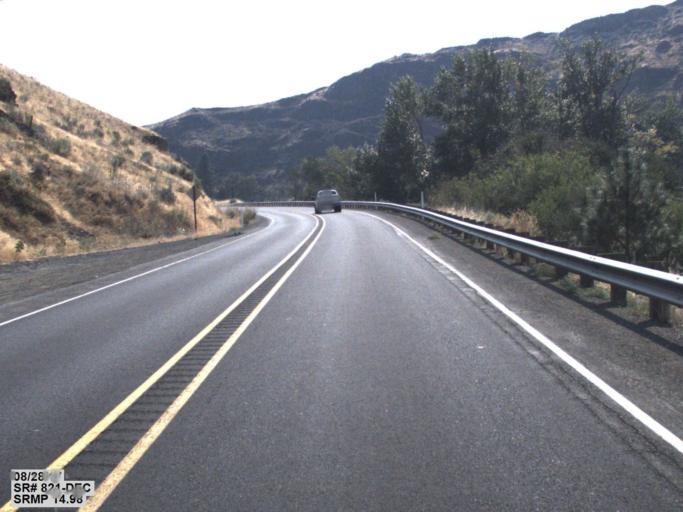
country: US
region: Washington
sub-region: Kittitas County
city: Kittitas
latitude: 46.8466
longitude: -120.4629
